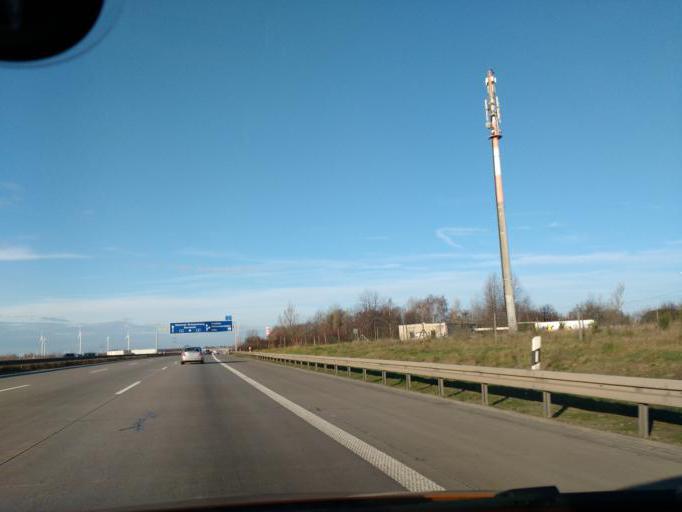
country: DE
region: Saxony-Anhalt
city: Hohenwarsleben
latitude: 52.1677
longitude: 11.5018
